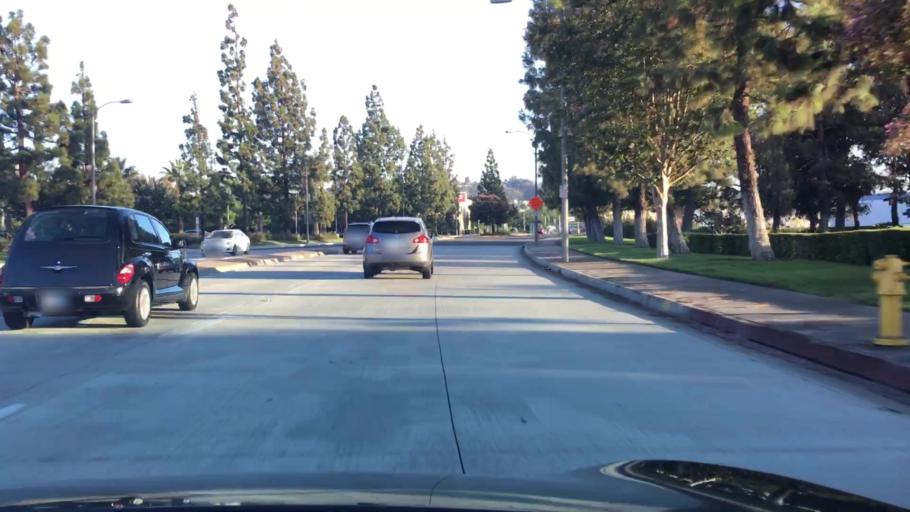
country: US
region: California
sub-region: Los Angeles County
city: Walnut
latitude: 34.0055
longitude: -117.8555
